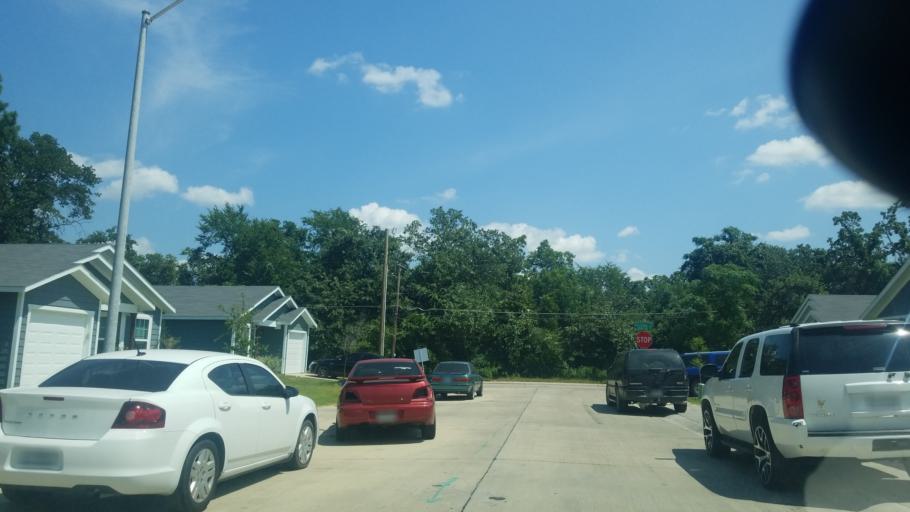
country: US
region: Texas
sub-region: Dallas County
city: Hutchins
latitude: 32.7166
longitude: -96.7456
